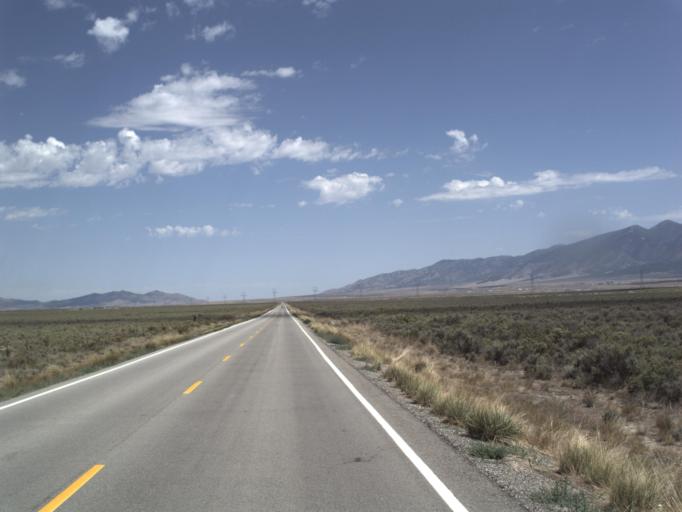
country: US
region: Utah
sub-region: Tooele County
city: Tooele
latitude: 40.2274
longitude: -112.4039
